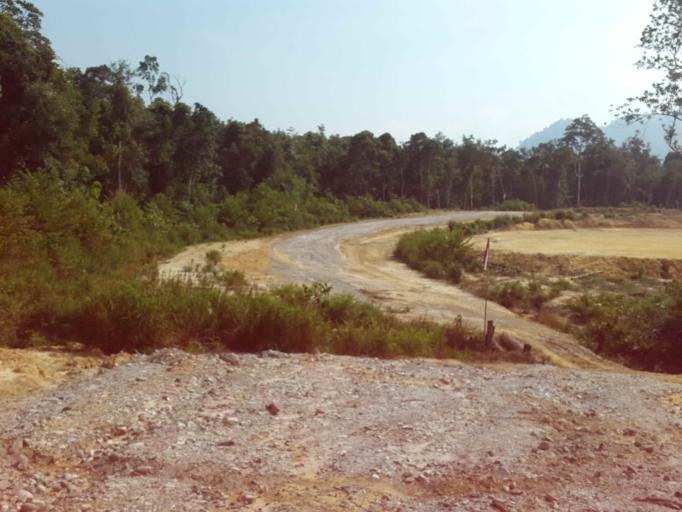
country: MY
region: Sarawak
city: Simanggang
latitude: 0.7726
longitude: 111.5800
